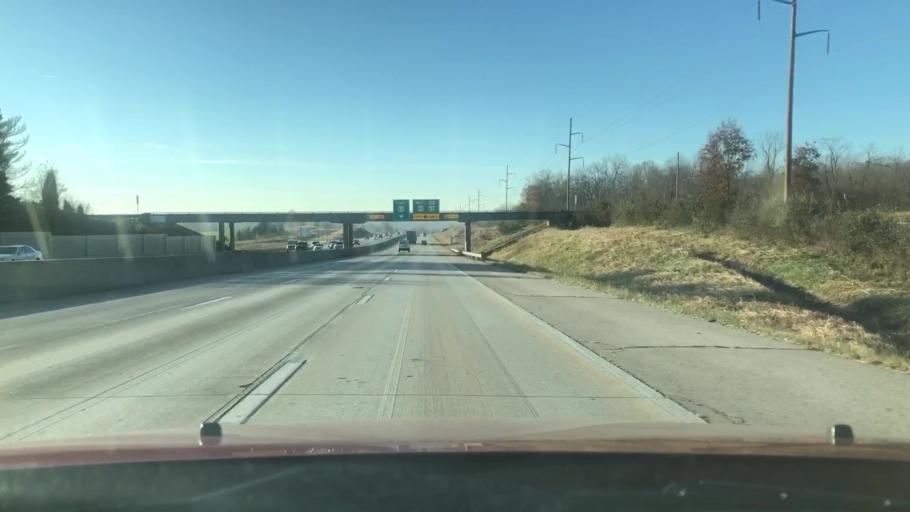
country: US
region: Missouri
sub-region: Greene County
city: Springfield
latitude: 37.1462
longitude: -93.2247
